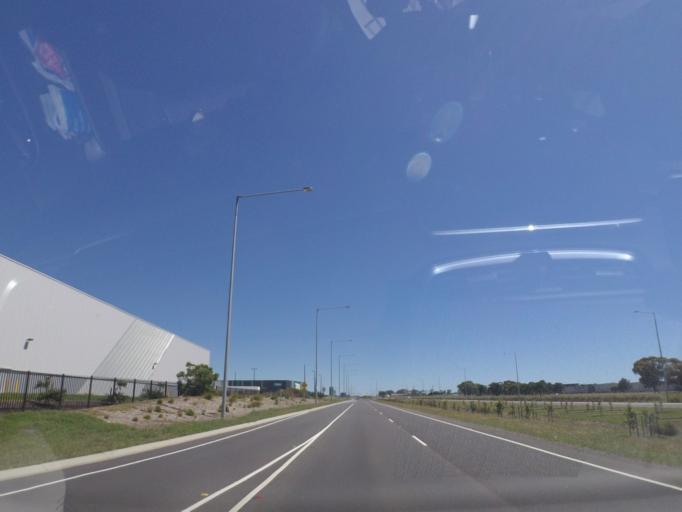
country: AU
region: Victoria
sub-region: Hume
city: Tullamarine
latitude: -37.6965
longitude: 144.8666
